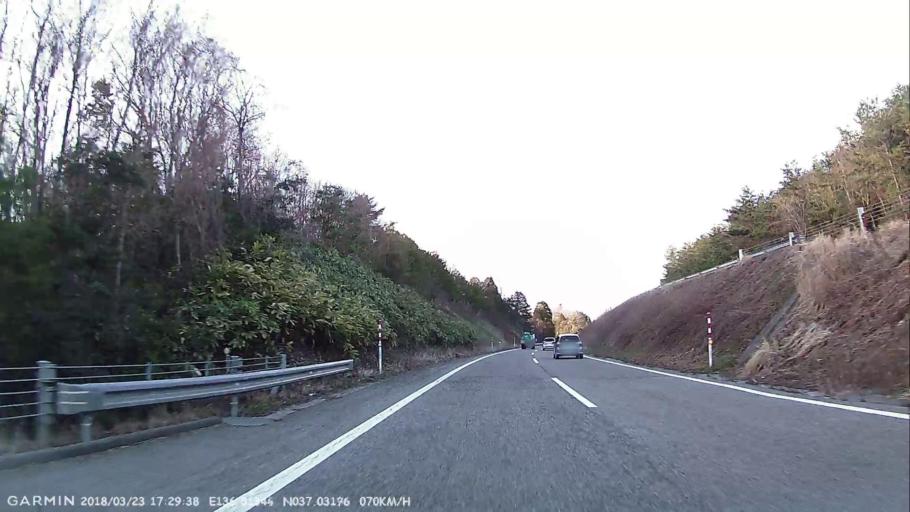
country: JP
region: Ishikawa
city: Hakui
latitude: 37.0321
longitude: 136.8135
